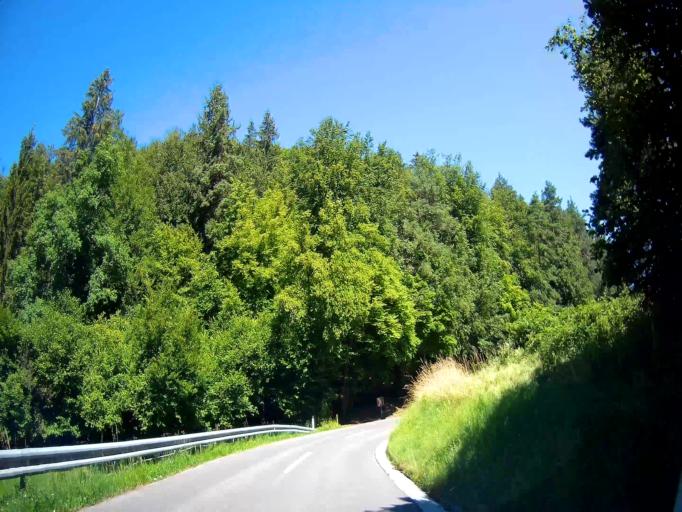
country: AT
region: Carinthia
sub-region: Politischer Bezirk Klagenfurt Land
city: Maria Worth
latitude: 46.5938
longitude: 14.1580
